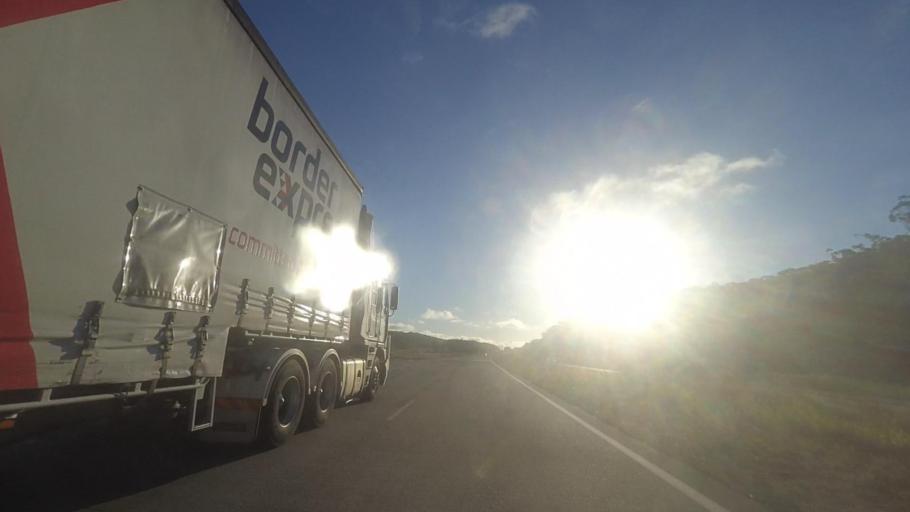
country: AU
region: New South Wales
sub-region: Great Lakes
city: Bulahdelah
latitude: -32.5213
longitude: 152.2028
